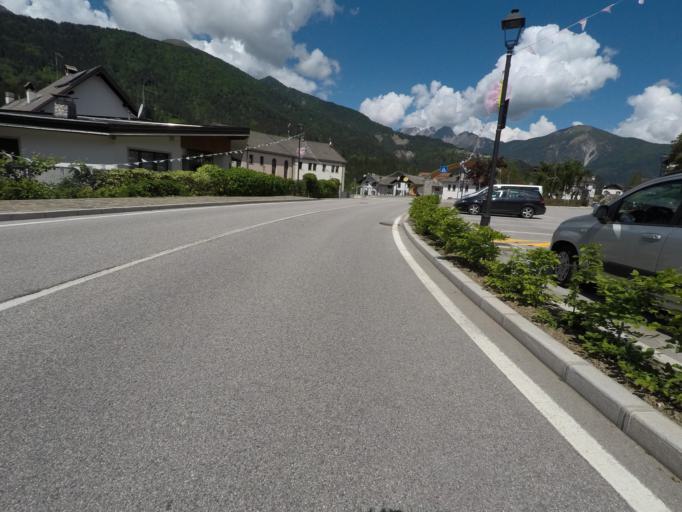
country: IT
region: Friuli Venezia Giulia
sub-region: Provincia di Udine
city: Ovaro
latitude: 46.4829
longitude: 12.8666
